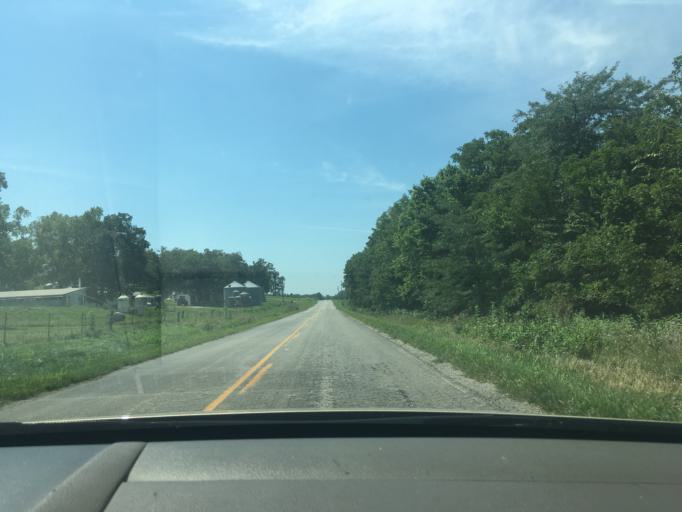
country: US
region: Missouri
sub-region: Gentry County
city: Stanberry
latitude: 40.2281
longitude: -94.7168
